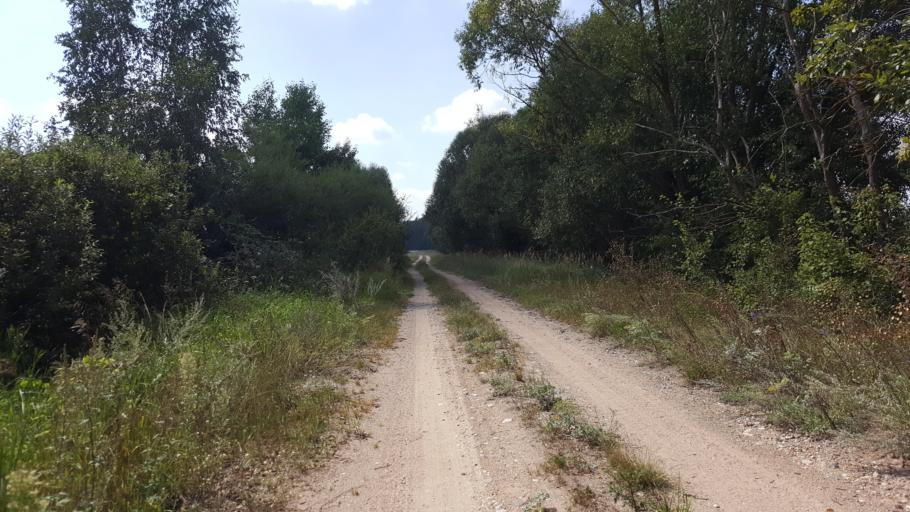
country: PL
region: Podlasie
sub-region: Powiat hajnowski
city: Hajnowka
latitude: 52.5746
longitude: 23.5658
